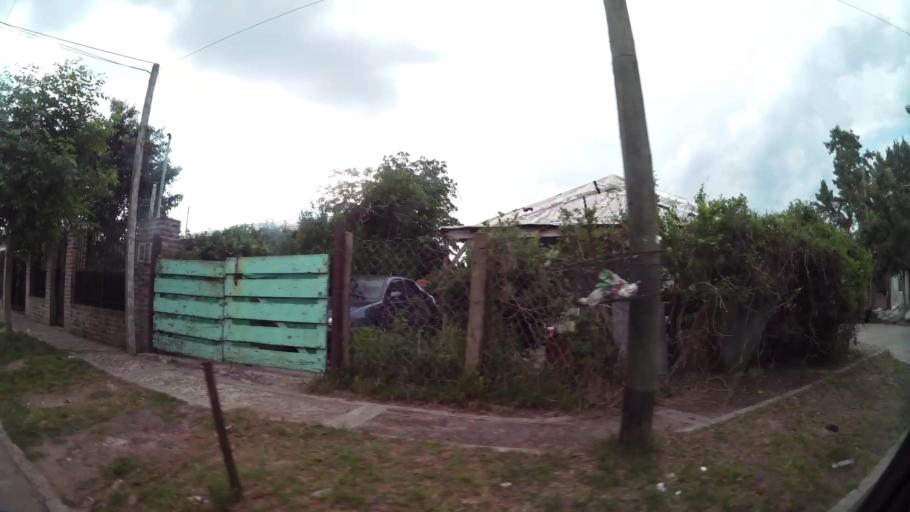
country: AR
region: Buenos Aires
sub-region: Partido de Tigre
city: Tigre
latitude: -34.4774
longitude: -58.6013
